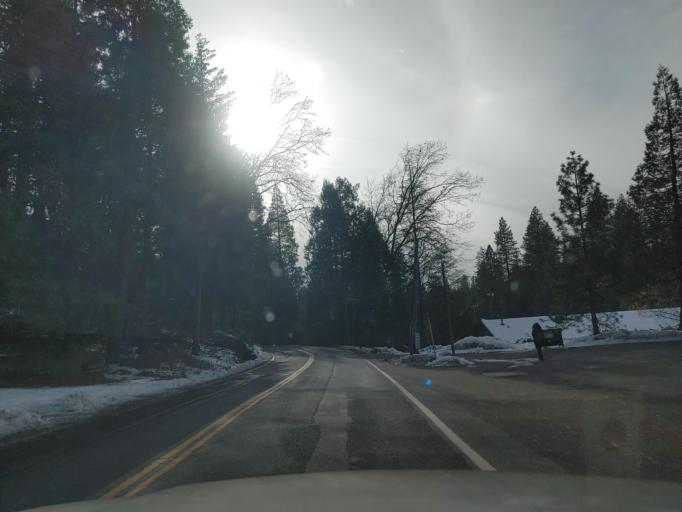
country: US
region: California
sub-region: Tuolumne County
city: Twain Harte
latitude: 38.0373
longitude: -120.2305
